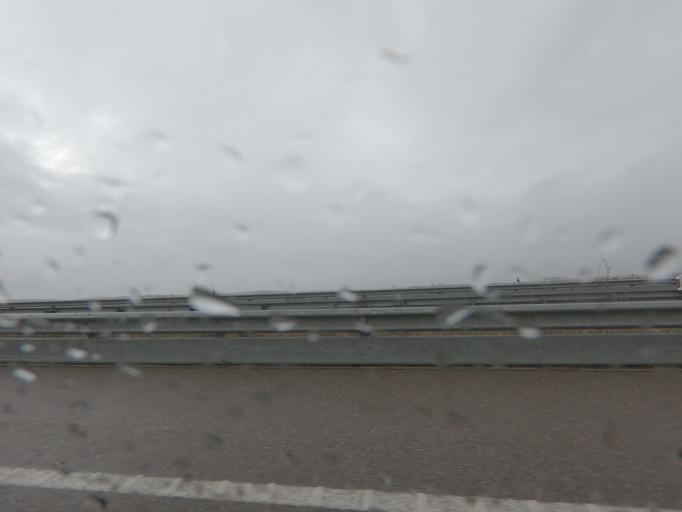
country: ES
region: Extremadura
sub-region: Provincia de Badajoz
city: Badajoz
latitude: 38.9155
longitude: -6.9629
